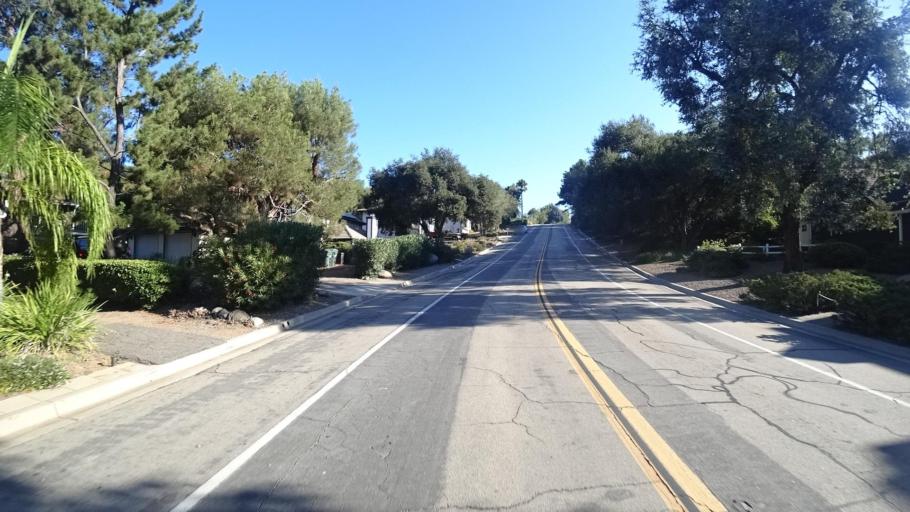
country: US
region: California
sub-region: San Diego County
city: Hidden Meadows
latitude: 33.2164
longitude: -117.1140
